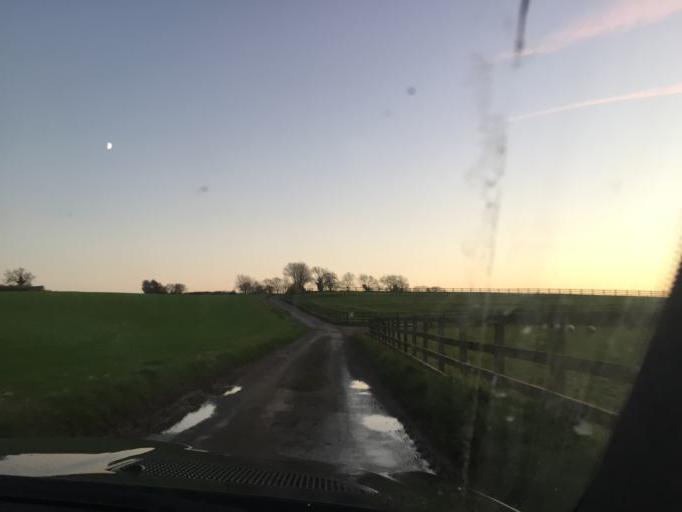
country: GB
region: England
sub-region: Northamptonshire
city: Brackley
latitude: 52.0918
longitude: -1.1119
